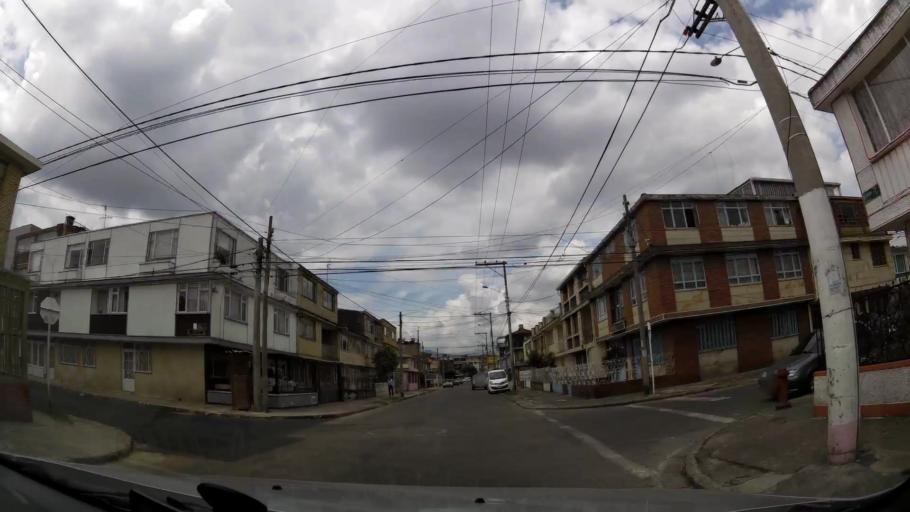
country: CO
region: Bogota D.C.
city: Bogota
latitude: 4.5961
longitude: -74.0991
